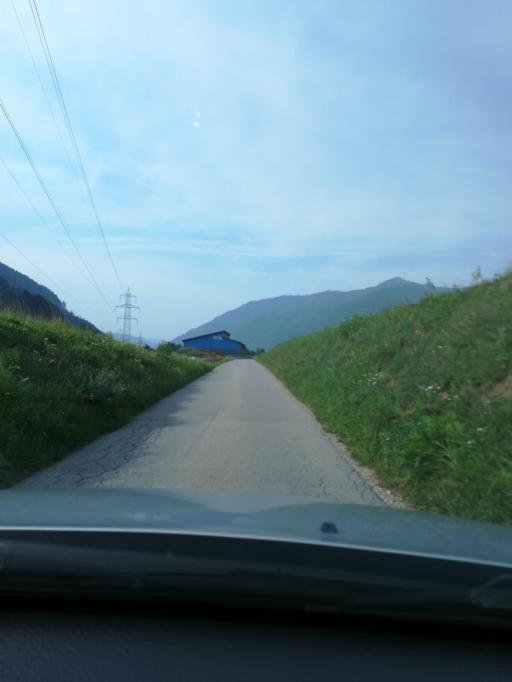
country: AT
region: Styria
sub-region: Politischer Bezirk Murtal
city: Sankt Georgen ob Judenburg
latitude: 47.2092
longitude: 14.4554
